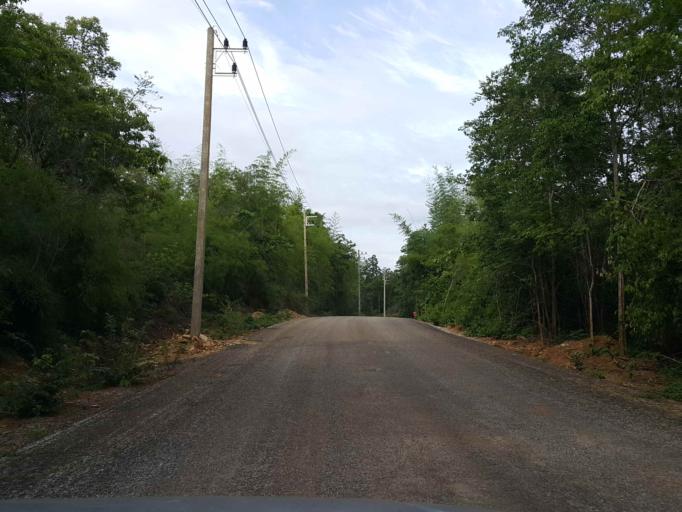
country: TH
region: Sukhothai
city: Thung Saliam
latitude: 17.2606
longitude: 99.5153
